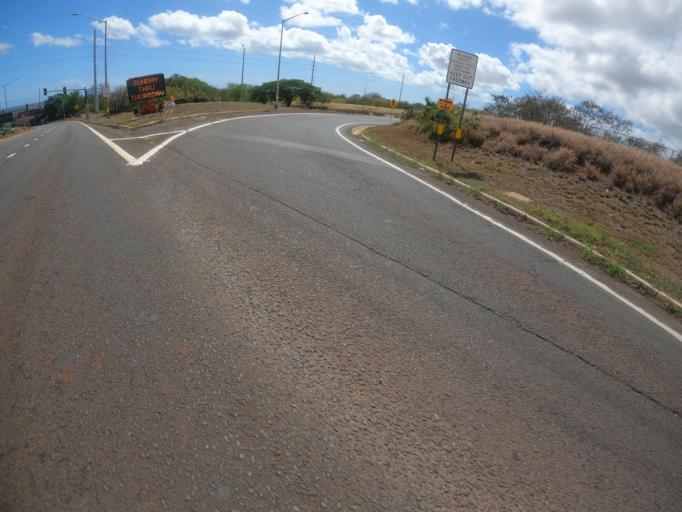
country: US
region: Hawaii
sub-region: Honolulu County
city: Royal Kunia
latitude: 21.3853
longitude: -158.0333
